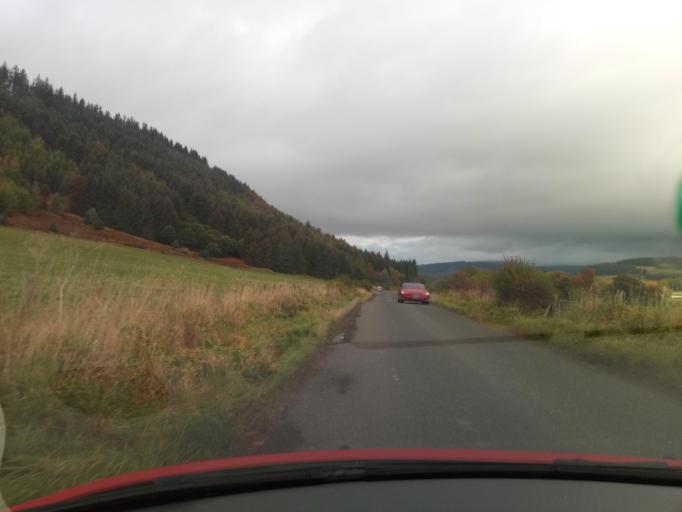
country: GB
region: Scotland
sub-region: The Scottish Borders
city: Innerleithen
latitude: 55.6167
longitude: -3.0880
